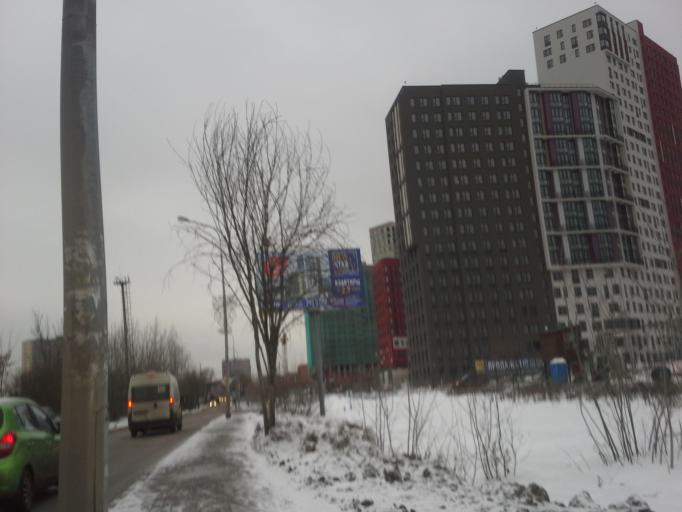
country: RU
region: Moskovskaya
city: Kommunarka
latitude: 55.5754
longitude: 37.4831
